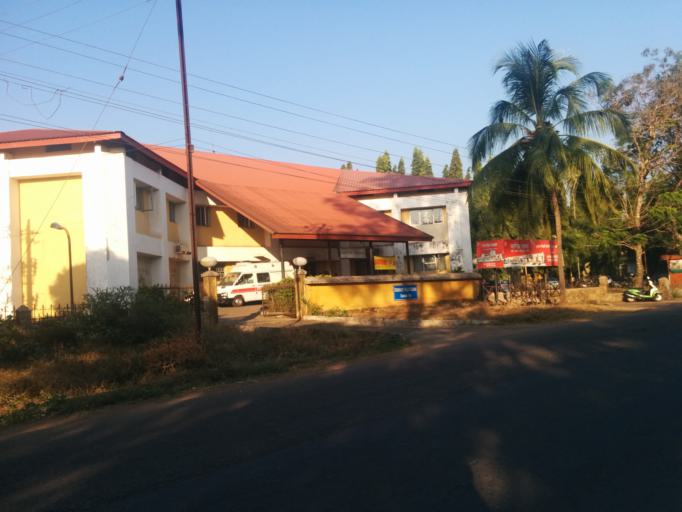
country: IN
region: Karnataka
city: Canacona
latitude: 15.0072
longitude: 74.0511
